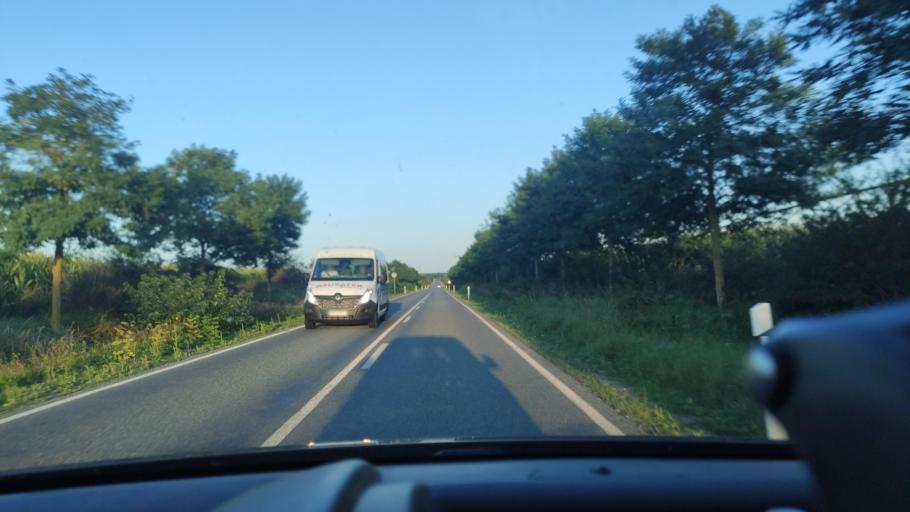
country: DE
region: Mecklenburg-Vorpommern
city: Krakow am See
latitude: 53.6167
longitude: 12.3921
